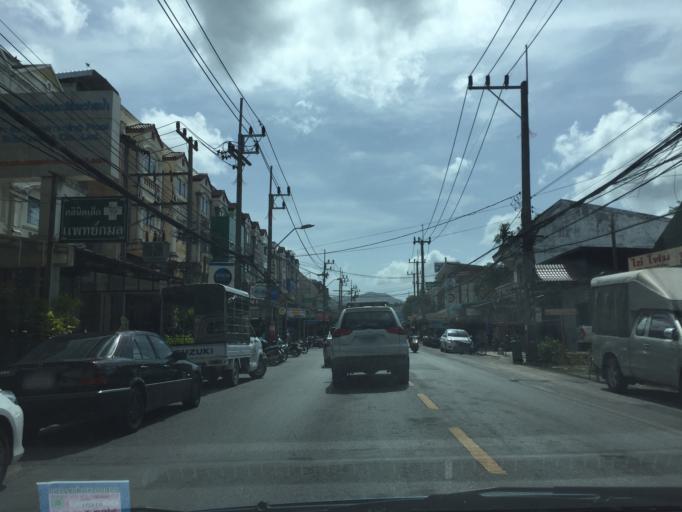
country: TH
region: Phuket
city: Wichit
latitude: 7.9020
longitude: 98.3793
